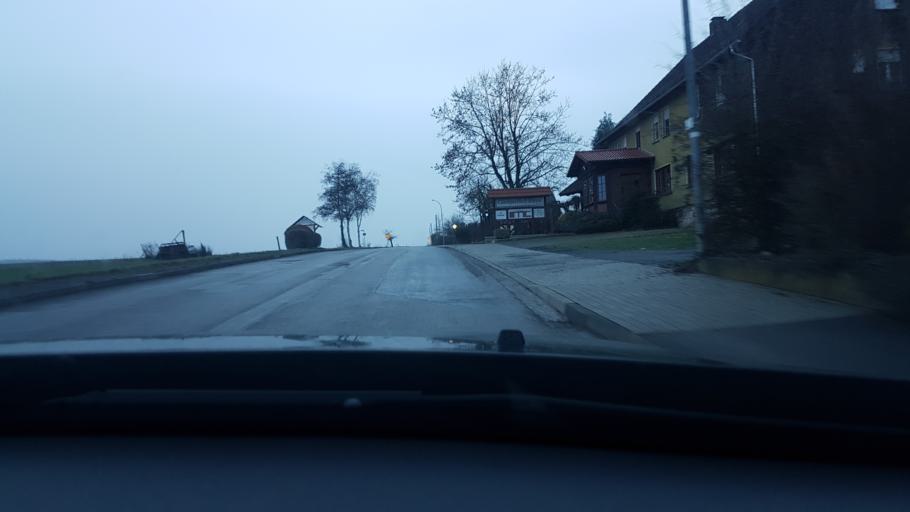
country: DE
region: Hesse
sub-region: Regierungsbezirk Kassel
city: Korbach
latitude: 51.3302
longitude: 8.9091
